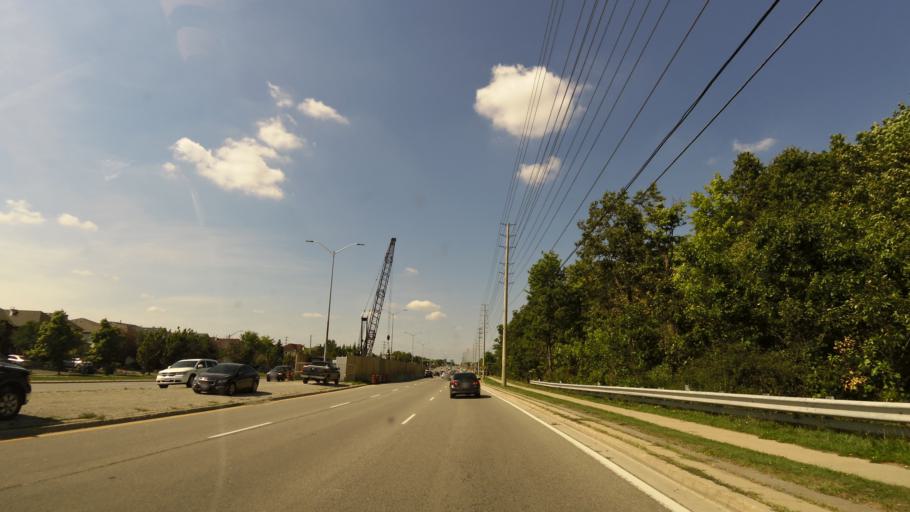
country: CA
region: Ontario
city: Mississauga
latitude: 43.5766
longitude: -79.7305
